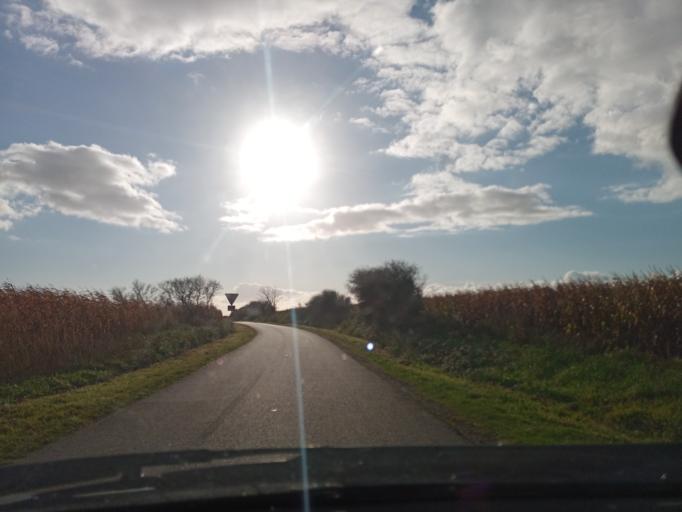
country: FR
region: Brittany
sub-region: Departement du Finistere
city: Plouhinec
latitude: 48.0239
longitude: -4.5082
